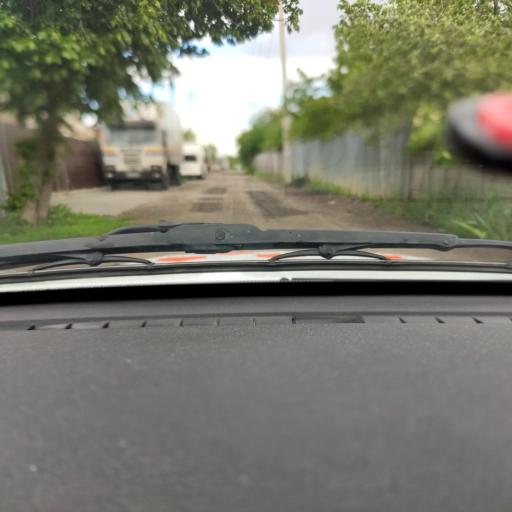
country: RU
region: Voronezj
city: Podgornoye
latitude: 51.7429
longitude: 39.1468
